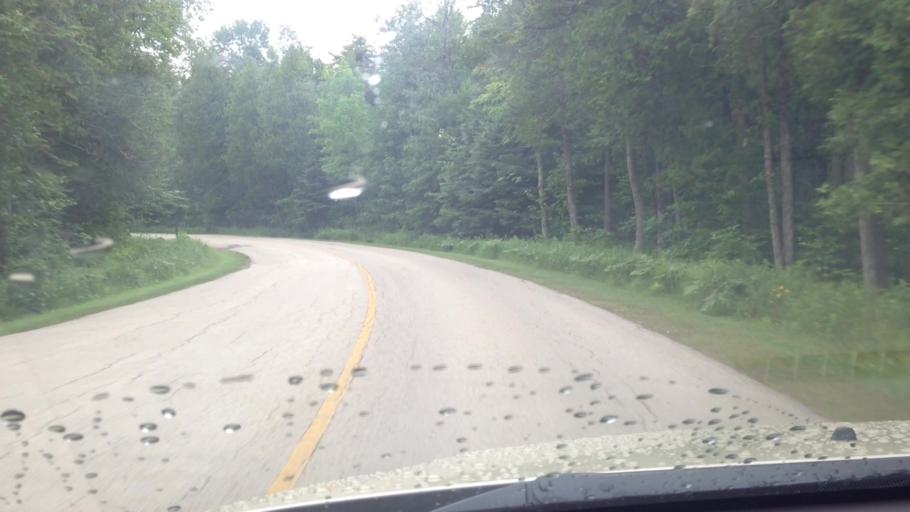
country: US
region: Michigan
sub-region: Menominee County
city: Menominee
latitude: 45.3919
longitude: -87.3656
